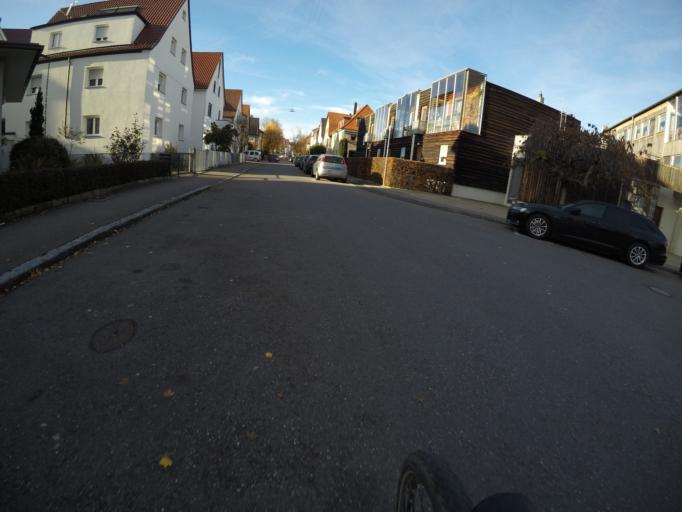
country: DE
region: Baden-Wuerttemberg
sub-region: Regierungsbezirk Stuttgart
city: Fellbach
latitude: 48.8112
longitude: 9.2791
